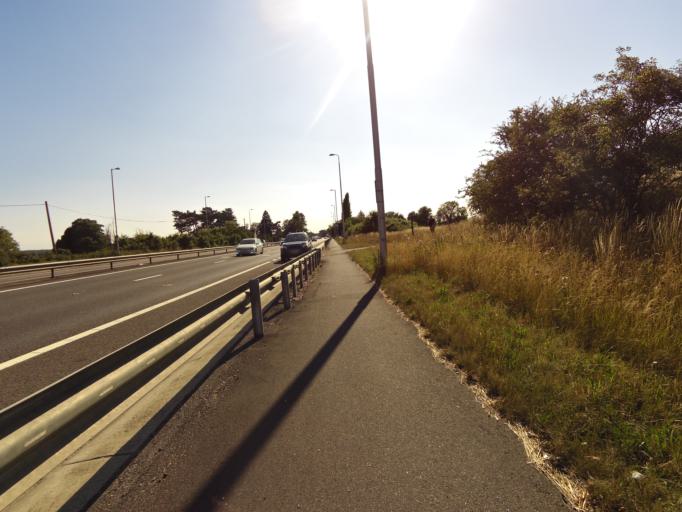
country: GB
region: England
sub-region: Essex
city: Kelvedon
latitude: 51.8233
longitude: 0.6796
